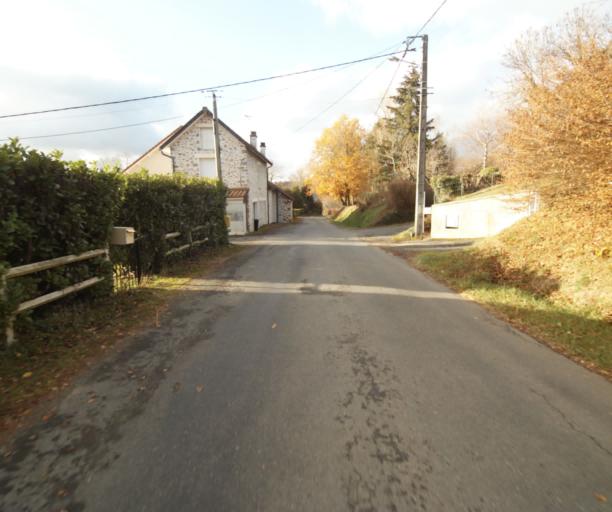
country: FR
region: Limousin
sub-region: Departement de la Correze
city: Laguenne
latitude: 45.2339
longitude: 1.7876
